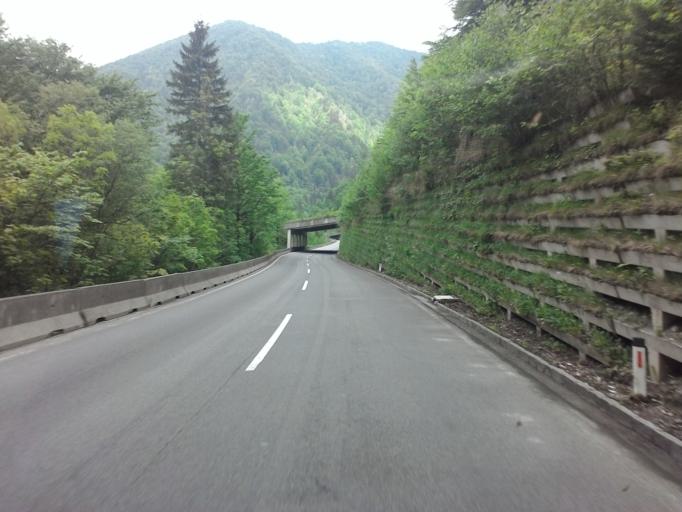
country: AT
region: Styria
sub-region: Politischer Bezirk Liezen
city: Altenmarkt bei Sankt Gallen
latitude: 47.7335
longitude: 14.6497
